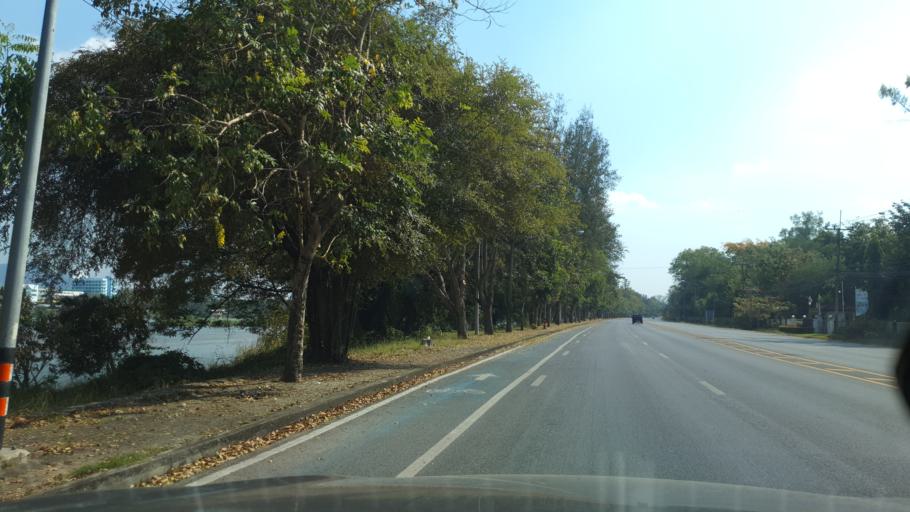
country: TH
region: Tak
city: Tak
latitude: 16.8753
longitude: 99.1171
